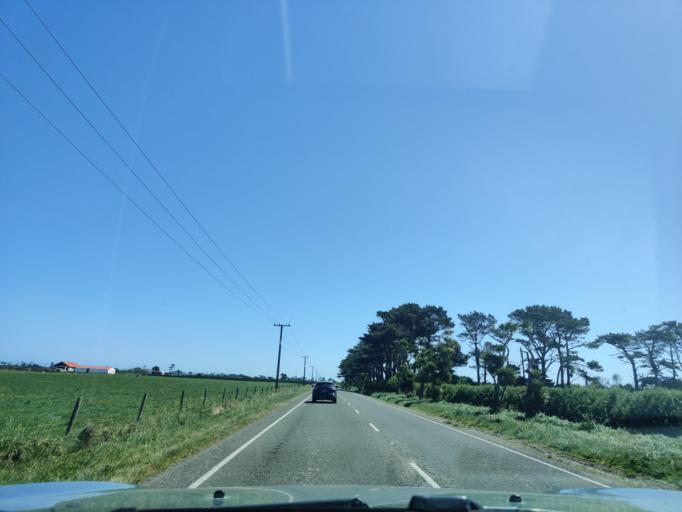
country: NZ
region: Taranaki
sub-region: South Taranaki District
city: Hawera
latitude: -39.5477
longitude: 174.0948
